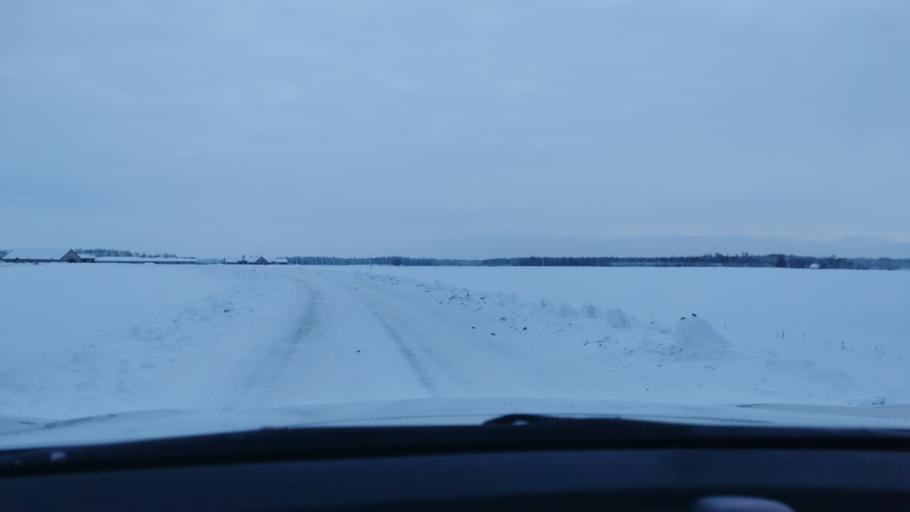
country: EE
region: Laeaene-Virumaa
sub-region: Haljala vald
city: Haljala
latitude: 59.4742
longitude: 26.3318
